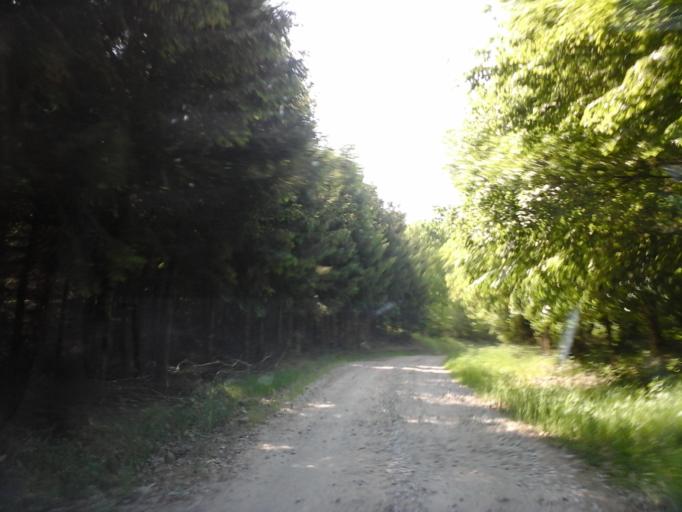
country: PL
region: West Pomeranian Voivodeship
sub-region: Powiat choszczenski
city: Recz
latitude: 53.3033
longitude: 15.5988
